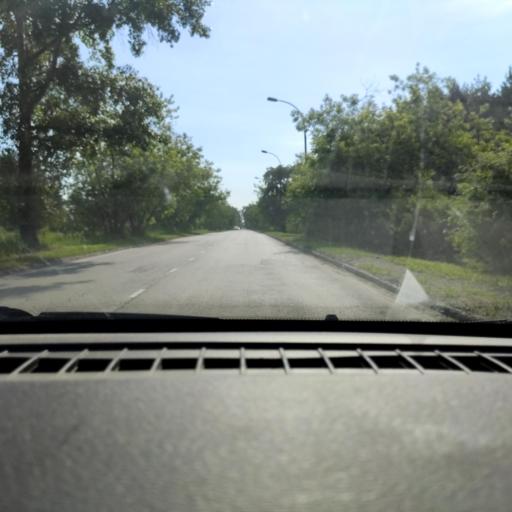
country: RU
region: Perm
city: Overyata
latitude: 57.9950
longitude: 55.9054
